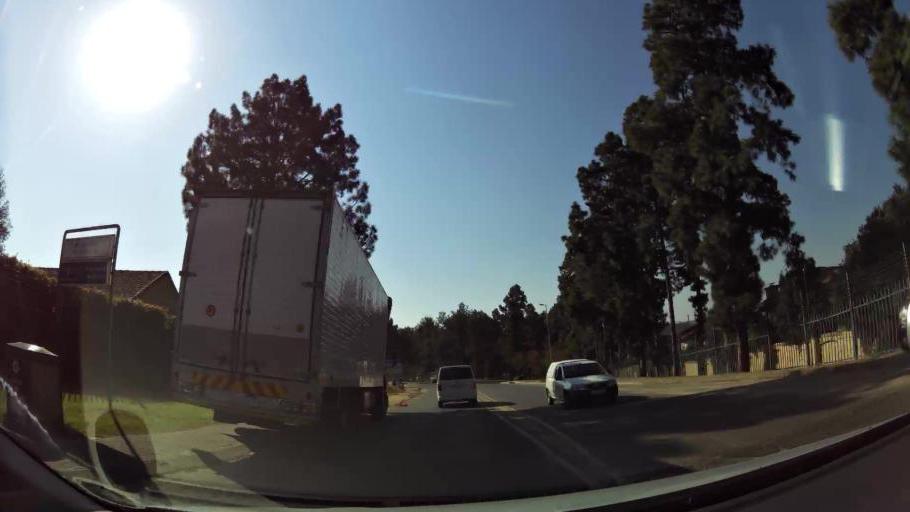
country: ZA
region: Gauteng
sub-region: City of Johannesburg Metropolitan Municipality
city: Modderfontein
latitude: -26.1035
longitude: 28.1513
